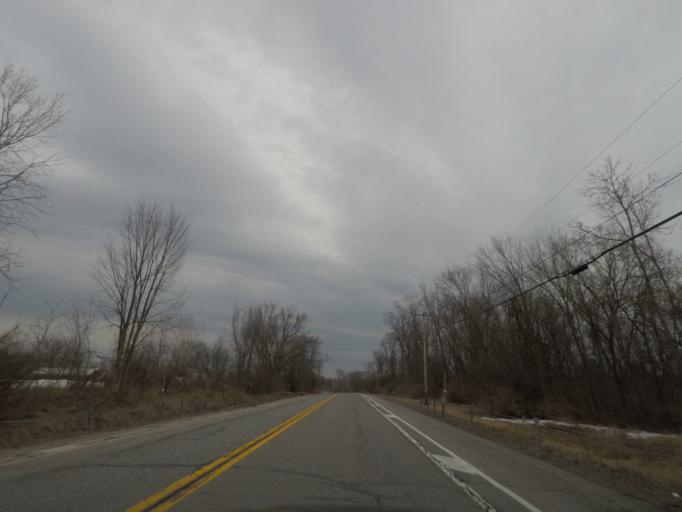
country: US
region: New York
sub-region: Washington County
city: Fort Edward
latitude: 43.2330
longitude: -73.5892
